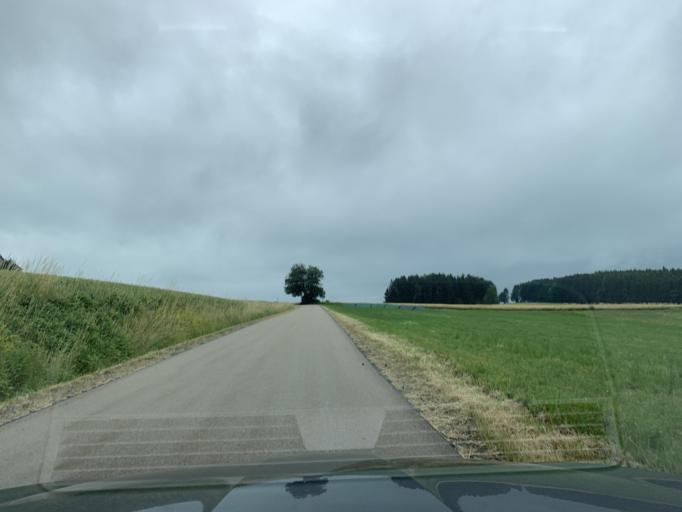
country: DE
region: Bavaria
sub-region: Upper Palatinate
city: Winklarn
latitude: 49.4187
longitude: 12.4489
